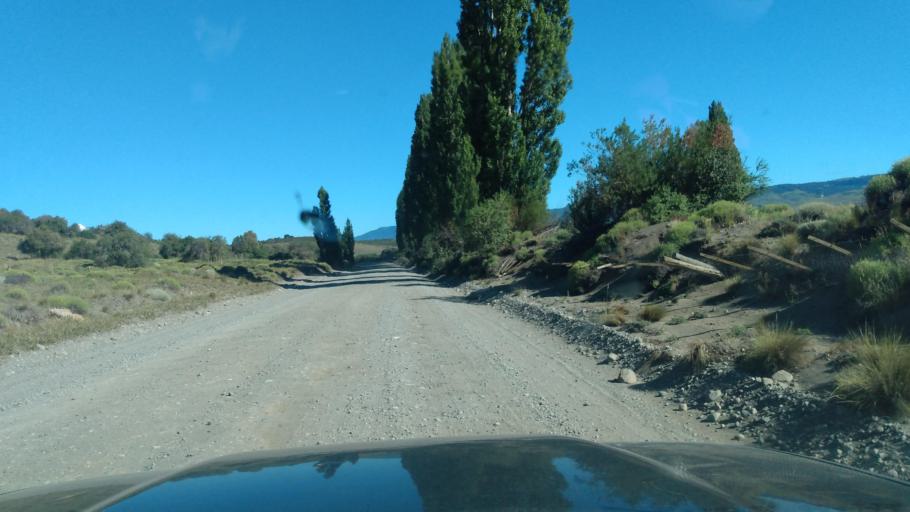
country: AR
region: Neuquen
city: Junin de los Andes
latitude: -39.8311
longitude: -71.1917
